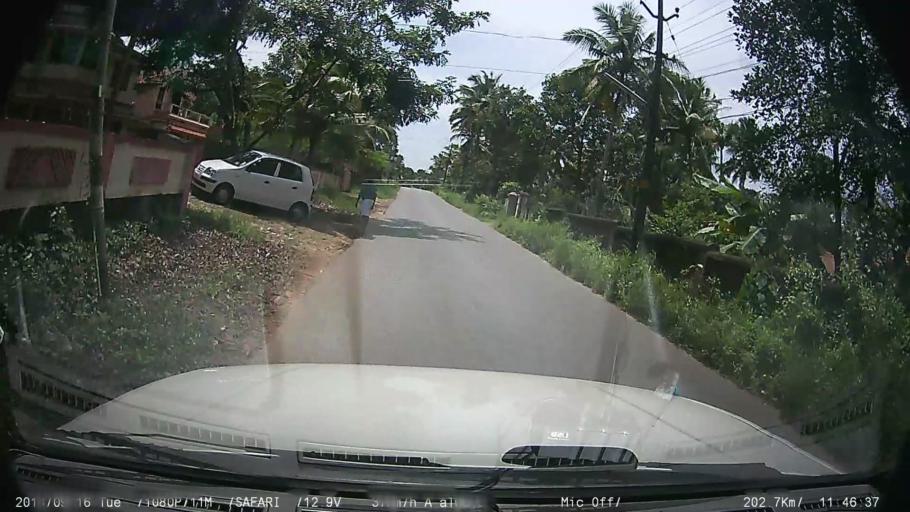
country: IN
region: Kerala
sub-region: Kottayam
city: Changanacheri
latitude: 9.4291
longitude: 76.5609
